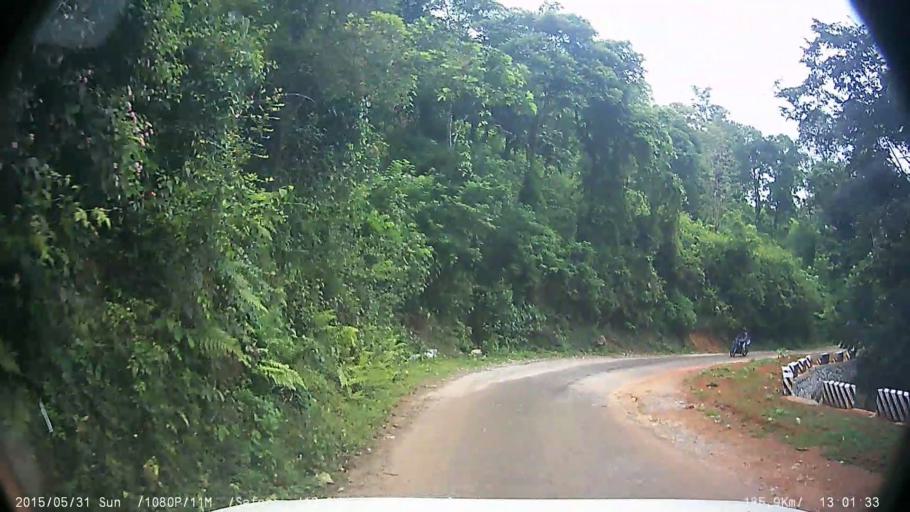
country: IN
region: Kerala
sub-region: Wayanad
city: Kalpetta
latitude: 11.5190
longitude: 76.1361
